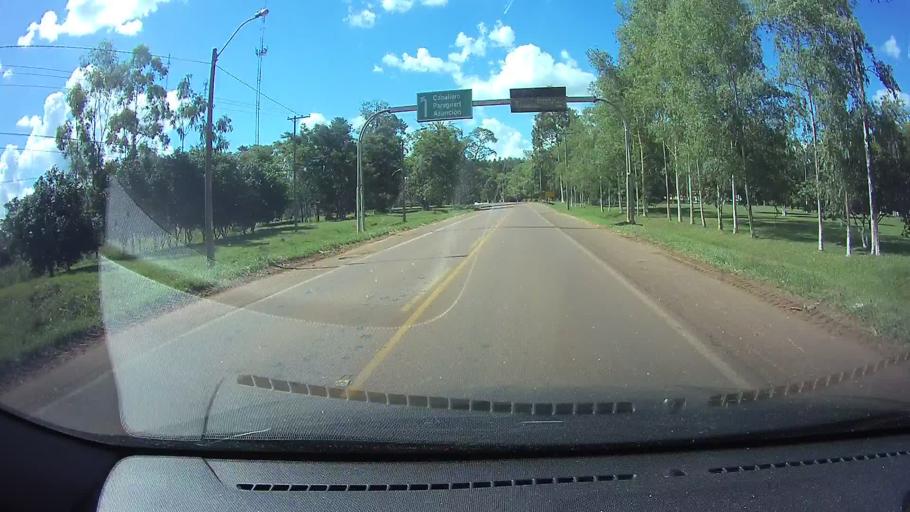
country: PY
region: Guaira
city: Coronel Martinez
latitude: -25.7720
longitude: -56.6518
